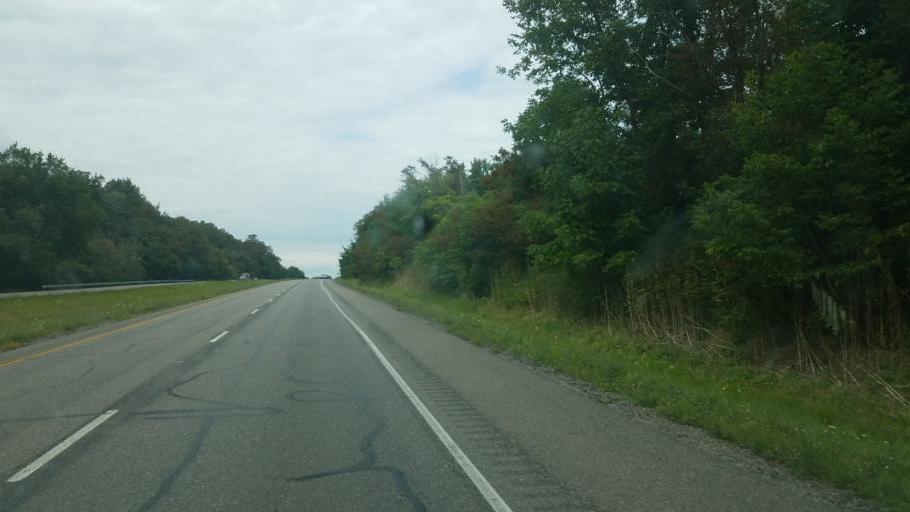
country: US
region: Ohio
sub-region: Columbiana County
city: Lisbon
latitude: 40.7904
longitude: -80.7414
